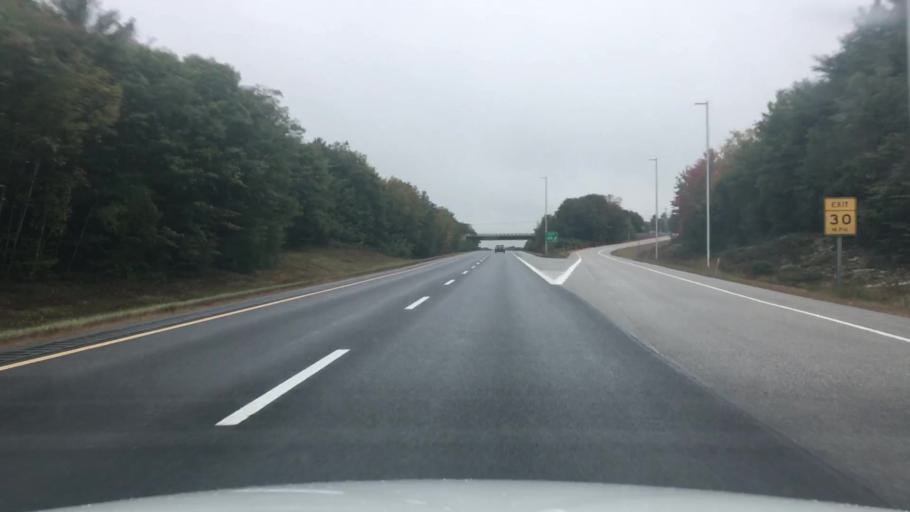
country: US
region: Maine
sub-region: Kennebec County
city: Gardiner
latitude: 44.1752
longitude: -69.8334
